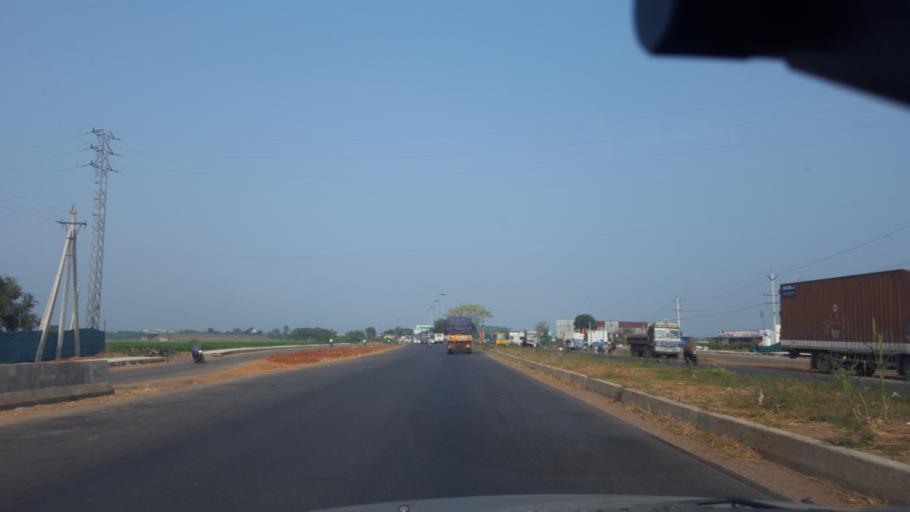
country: IN
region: Andhra Pradesh
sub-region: West Godavari
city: Eluru
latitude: 16.6741
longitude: 81.0196
